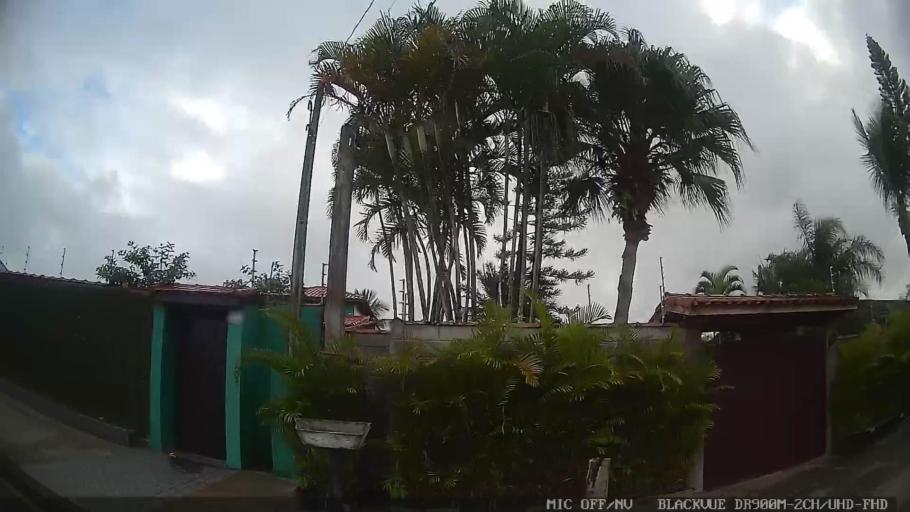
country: BR
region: Sao Paulo
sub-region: Itanhaem
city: Itanhaem
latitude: -24.2131
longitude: -46.8524
